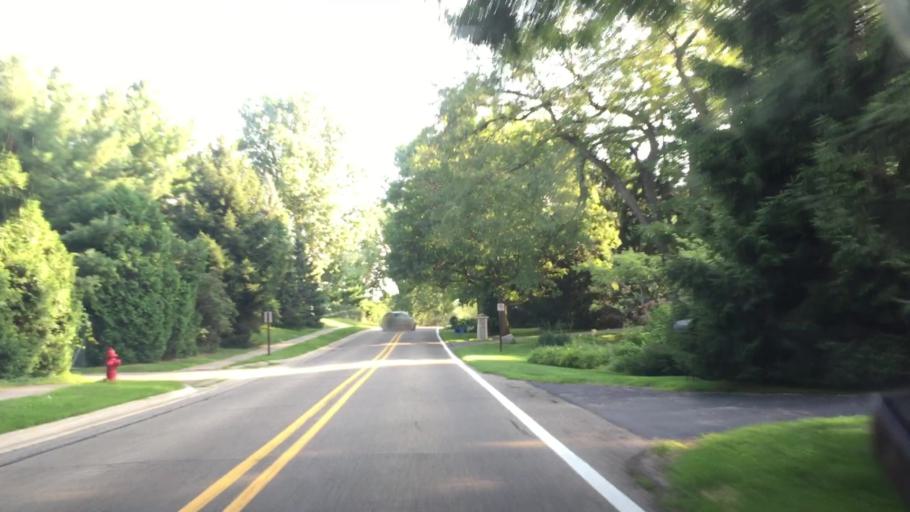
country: US
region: Michigan
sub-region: Oakland County
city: Bingham Farms
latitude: 42.5480
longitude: -83.2758
